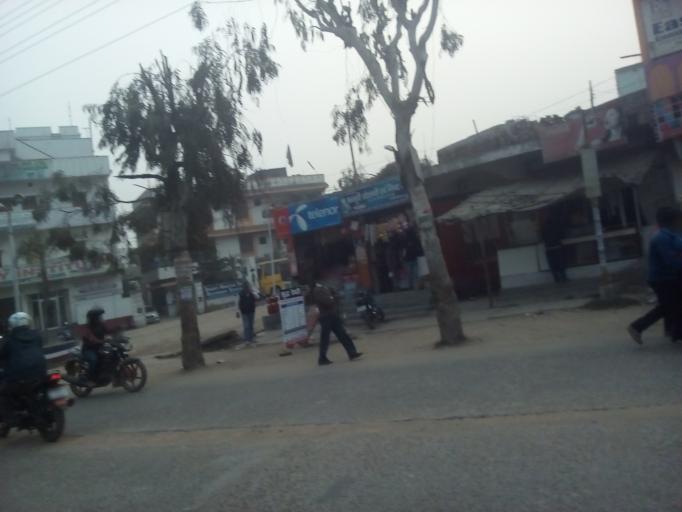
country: IN
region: Bihar
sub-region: Muzaffarpur
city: Muzaffarpur
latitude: 26.1073
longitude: 85.3974
